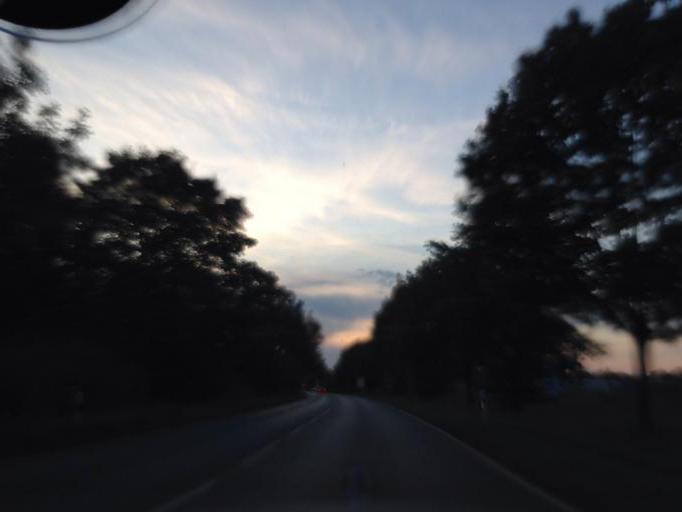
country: DE
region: Schleswig-Holstein
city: Delingsdorf
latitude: 53.6760
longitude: 10.2533
